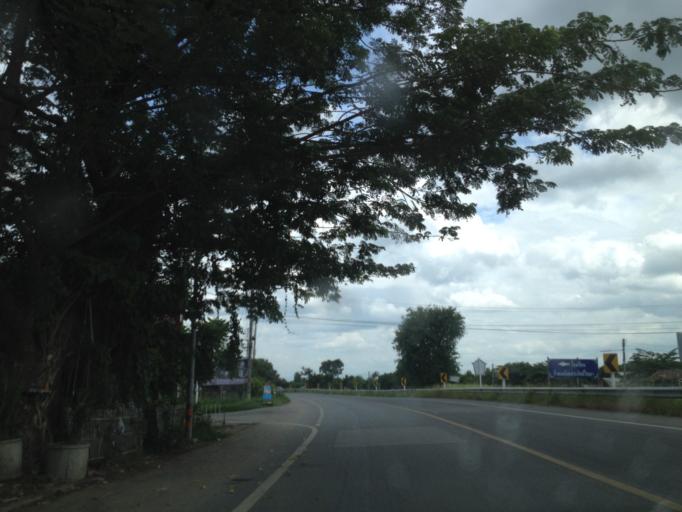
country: TH
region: Chiang Mai
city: San Pa Tong
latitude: 18.6341
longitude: 98.8515
